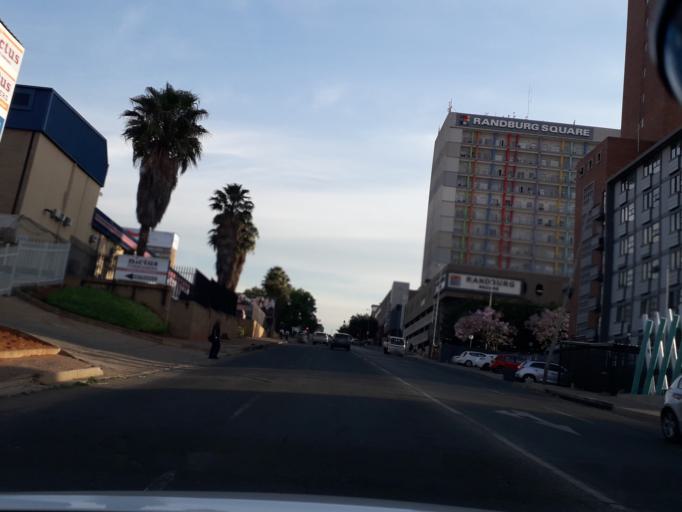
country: ZA
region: Gauteng
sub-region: City of Johannesburg Metropolitan Municipality
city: Johannesburg
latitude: -26.0904
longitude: 28.0047
